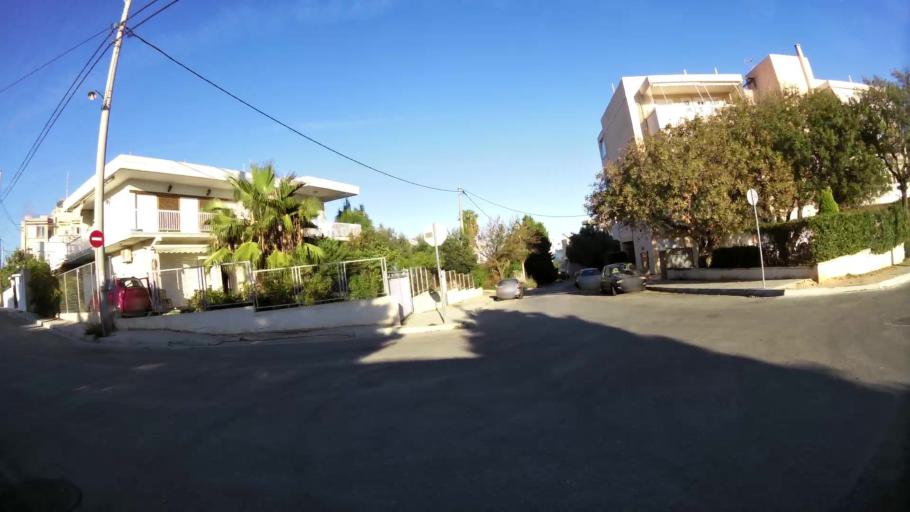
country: GR
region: Attica
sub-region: Nomarchia Anatolikis Attikis
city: Rafina
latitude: 38.0231
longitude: 24.0023
